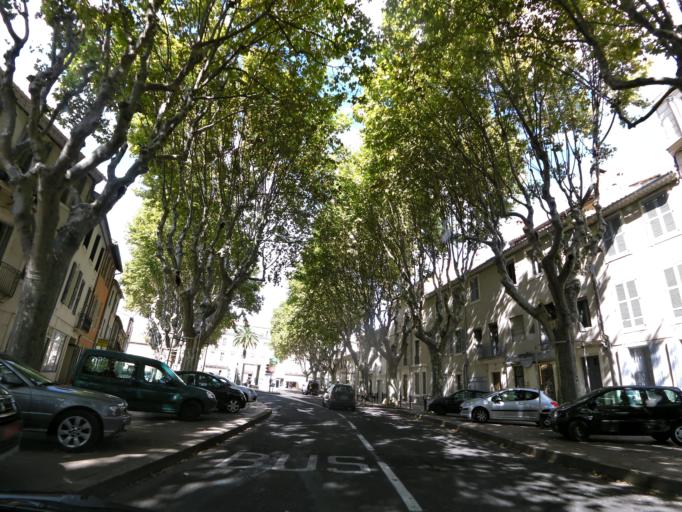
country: FR
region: Languedoc-Roussillon
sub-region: Departement du Gard
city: Nimes
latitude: 43.8362
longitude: 4.3660
